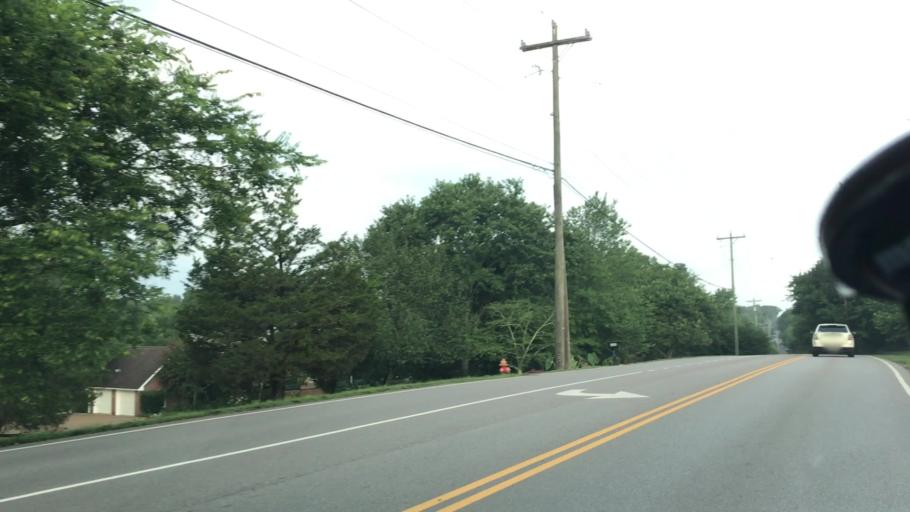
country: US
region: Tennessee
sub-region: Williamson County
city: Brentwood Estates
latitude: 36.0148
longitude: -86.7114
